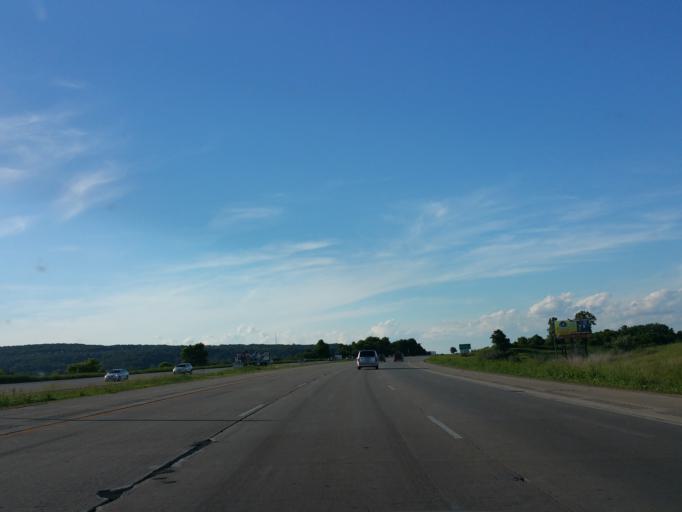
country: US
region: Wisconsin
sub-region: Columbia County
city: Portage
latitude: 43.4548
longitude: -89.4978
